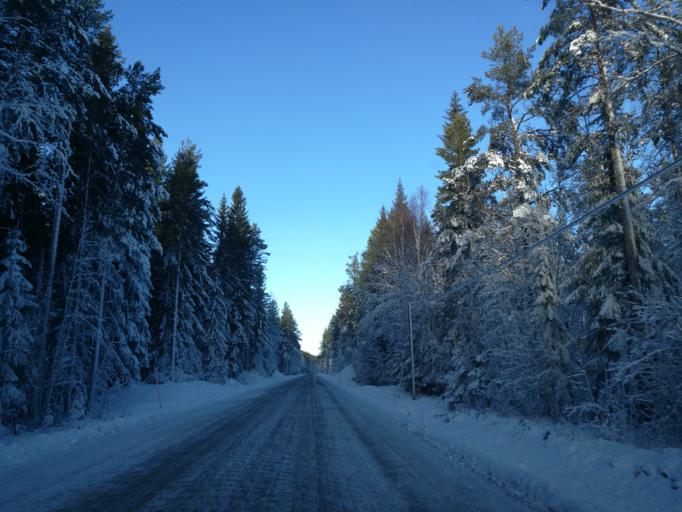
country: NO
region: Hedmark
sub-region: Grue
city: Kirkenaer
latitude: 60.4958
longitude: 12.5634
